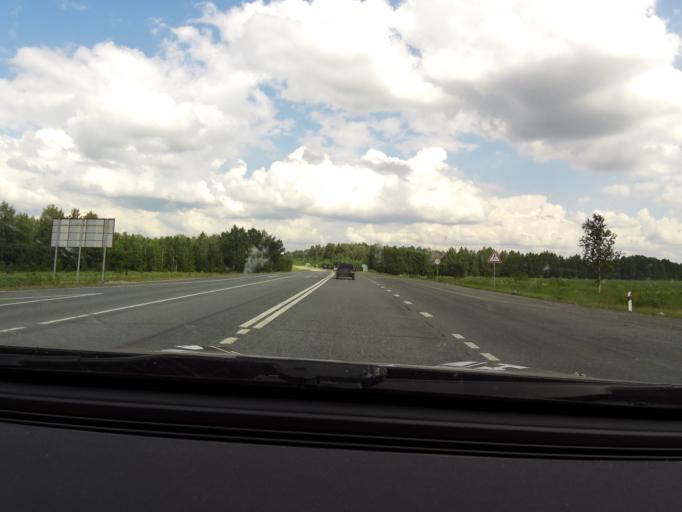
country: RU
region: Sverdlovsk
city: Bisert'
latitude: 56.7971
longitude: 58.6870
